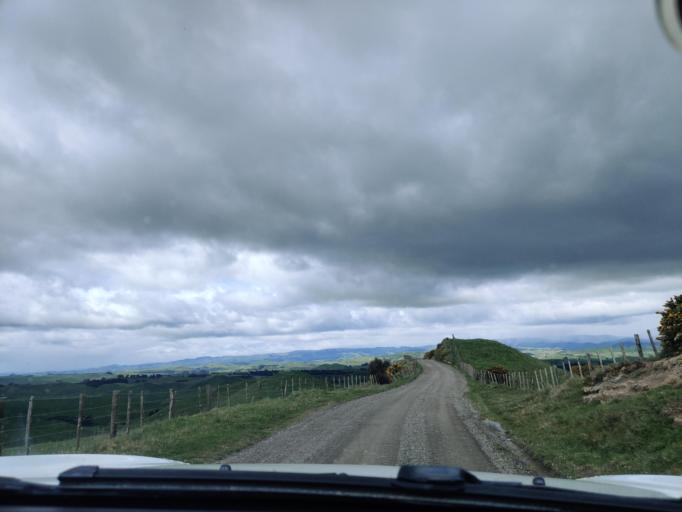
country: NZ
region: Manawatu-Wanganui
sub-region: Palmerston North City
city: Palmerston North
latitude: -40.2848
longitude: 175.8616
